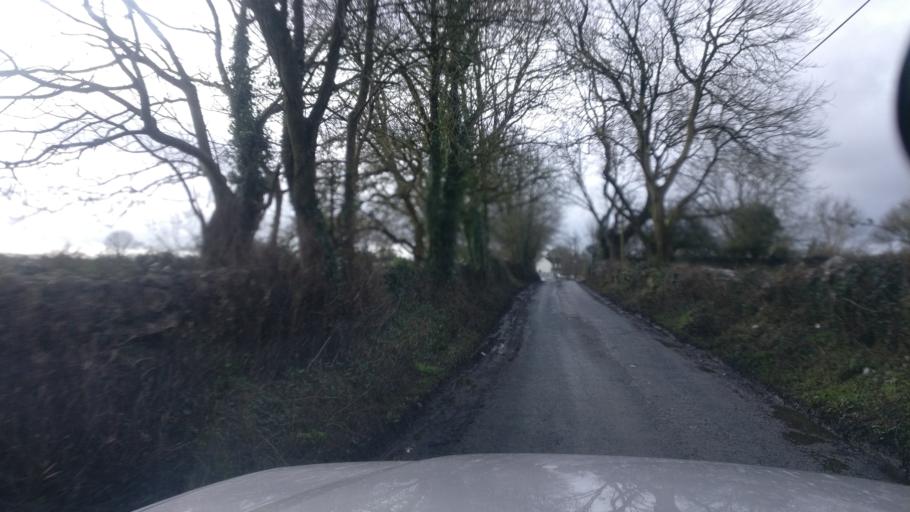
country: IE
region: Connaught
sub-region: County Galway
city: Athenry
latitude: 53.2652
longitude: -8.7926
